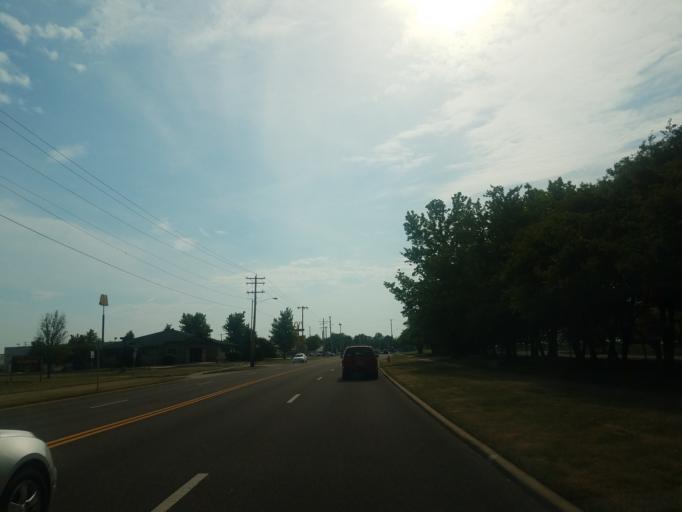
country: US
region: Illinois
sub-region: McLean County
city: Bloomington
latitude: 40.4506
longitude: -88.9895
